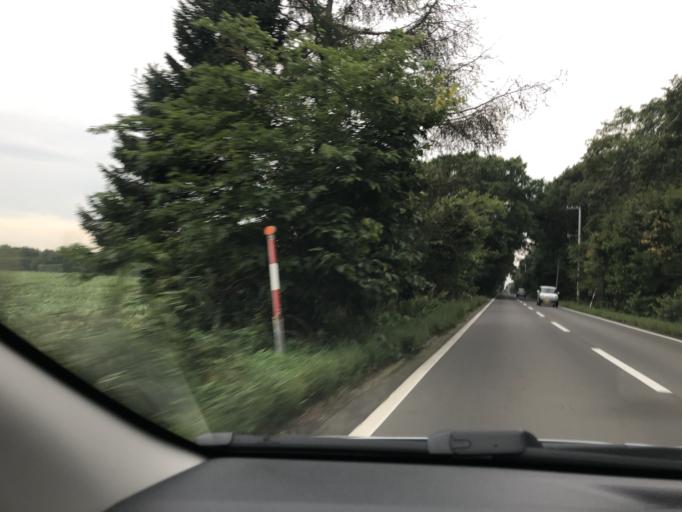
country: JP
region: Hokkaido
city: Chitose
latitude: 42.8708
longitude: 141.7327
